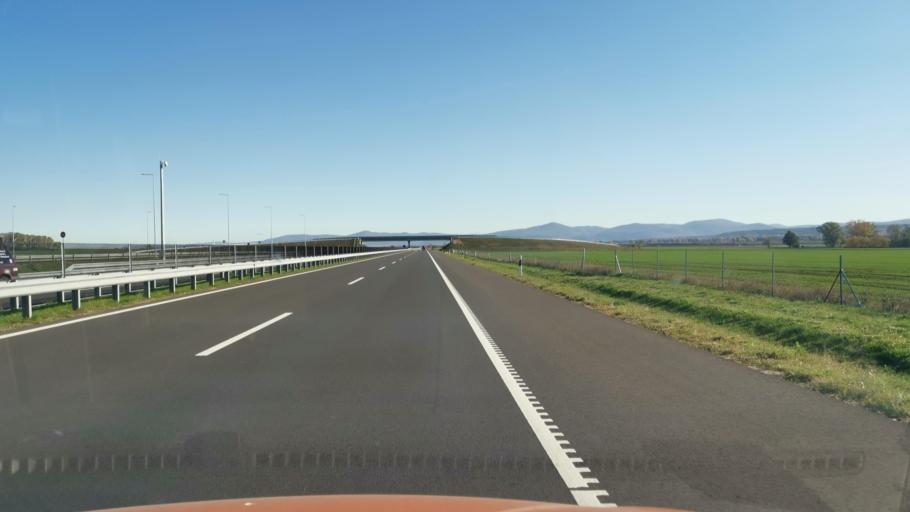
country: HU
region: Borsod-Abauj-Zemplen
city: Halmaj
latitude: 48.2933
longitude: 21.0359
